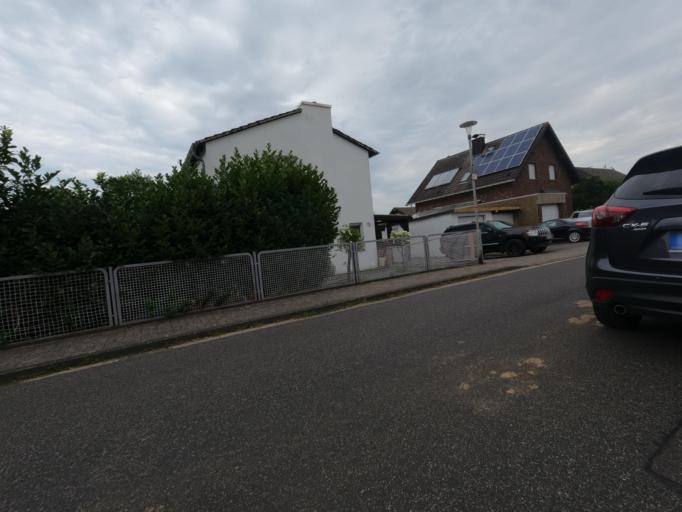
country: DE
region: North Rhine-Westphalia
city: Geilenkirchen
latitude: 50.9810
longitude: 6.1132
